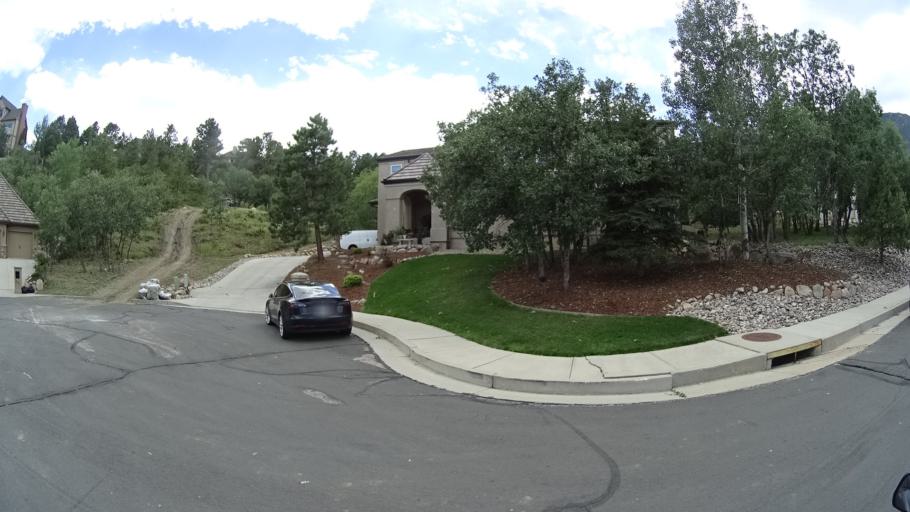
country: US
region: Colorado
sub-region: El Paso County
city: Fort Carson
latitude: 38.7677
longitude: -104.8329
